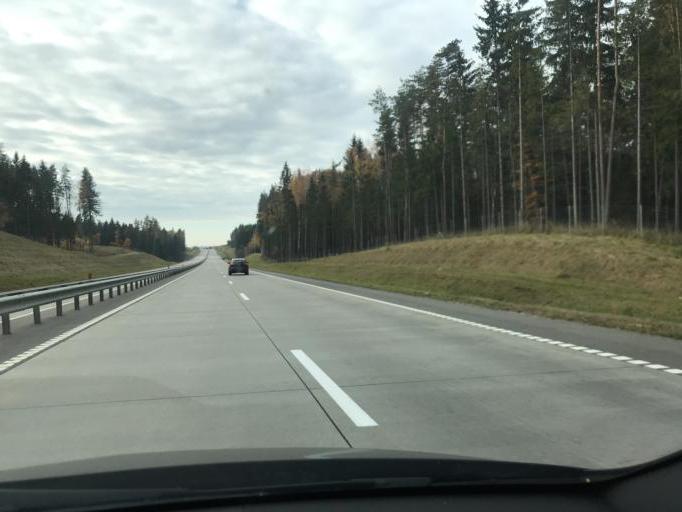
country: BY
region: Minsk
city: Rakaw
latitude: 53.9921
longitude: 27.1123
